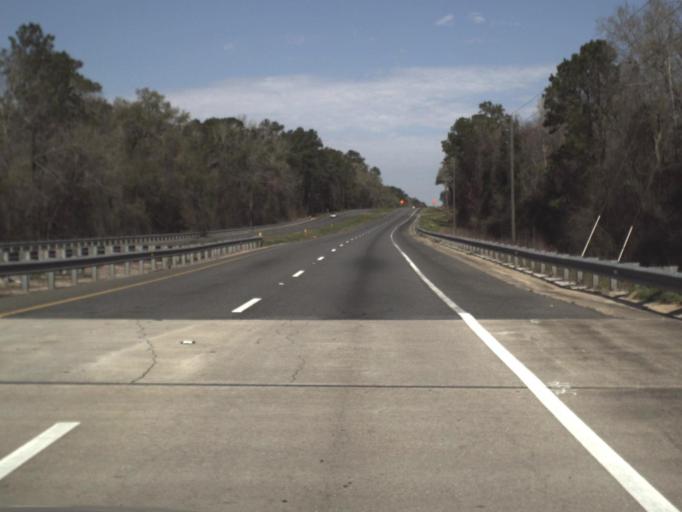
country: US
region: Florida
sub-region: Gadsden County
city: Havana
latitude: 30.5605
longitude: -84.3884
